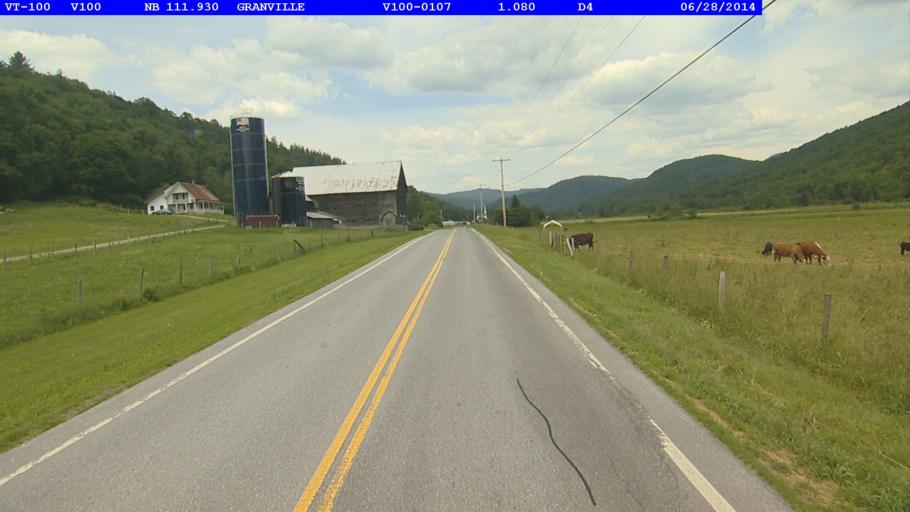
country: US
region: Vermont
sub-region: Orange County
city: Randolph
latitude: 43.9600
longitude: -72.8410
